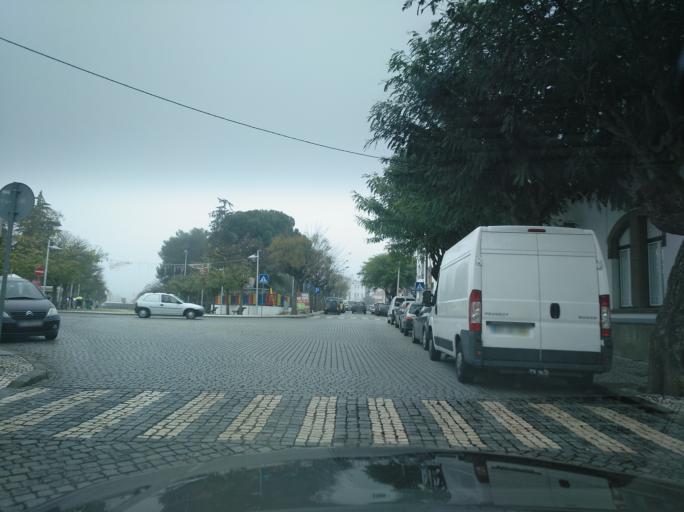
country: PT
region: Portalegre
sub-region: Campo Maior
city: Campo Maior
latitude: 39.0142
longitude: -7.0676
